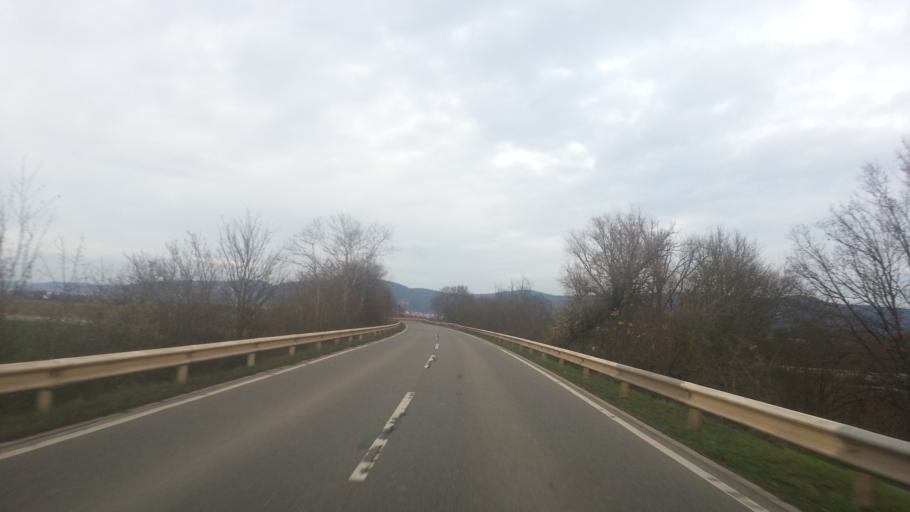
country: DE
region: Baden-Wuerttemberg
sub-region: Karlsruhe Region
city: Eppelheim
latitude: 49.4191
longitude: 8.6268
